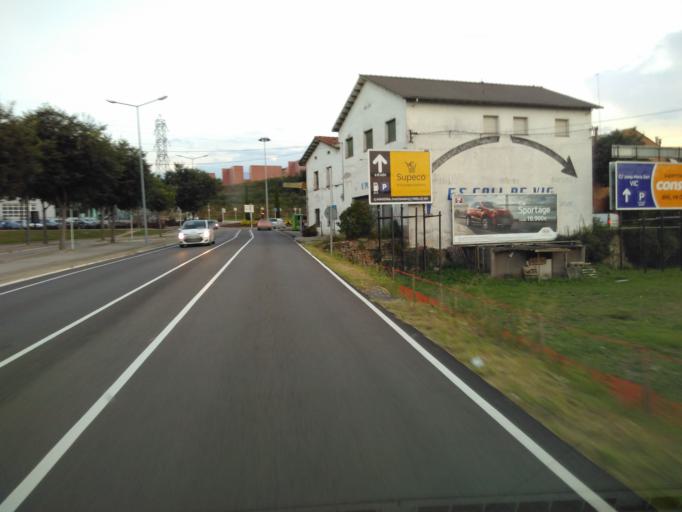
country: ES
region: Catalonia
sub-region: Provincia de Barcelona
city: Vic
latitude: 41.9386
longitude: 2.2551
